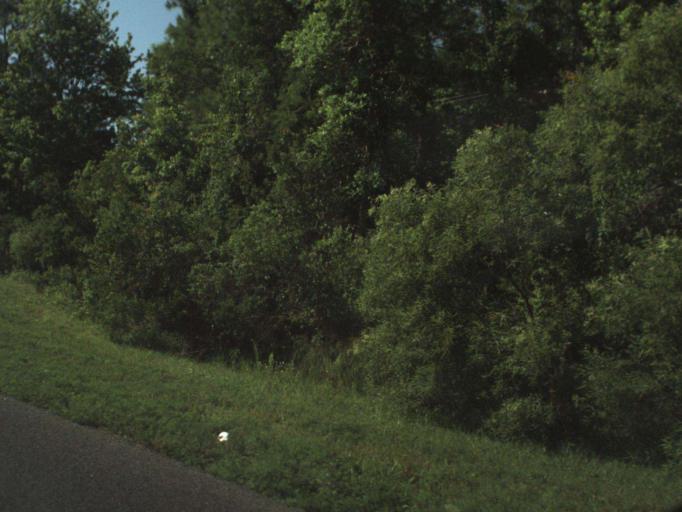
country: US
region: Florida
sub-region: Orange County
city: Bithlo
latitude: 28.5375
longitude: -81.0816
